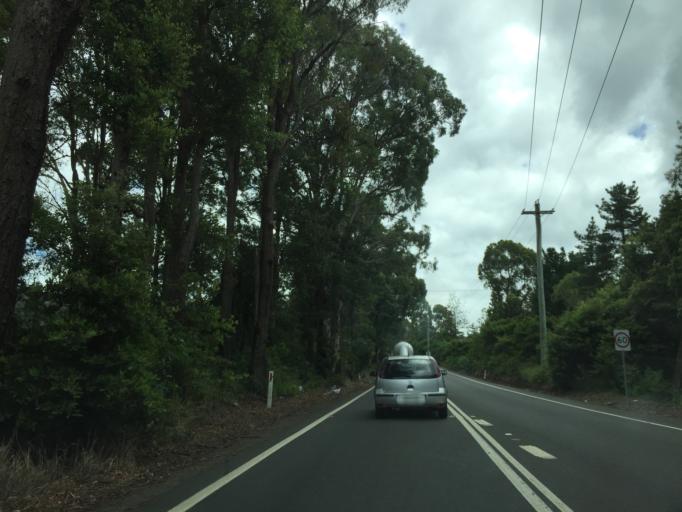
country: AU
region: New South Wales
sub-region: Hawkesbury
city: Richmond
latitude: -33.5464
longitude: 150.6492
